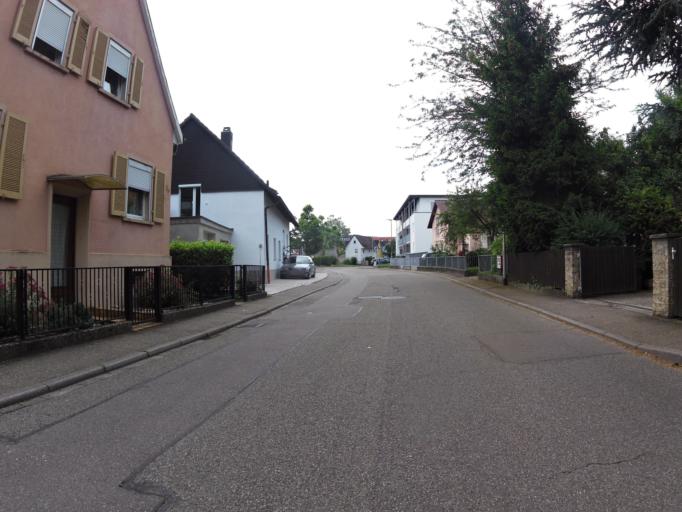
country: DE
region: Baden-Wuerttemberg
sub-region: Freiburg Region
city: Lahr
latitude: 48.3455
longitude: 7.8397
